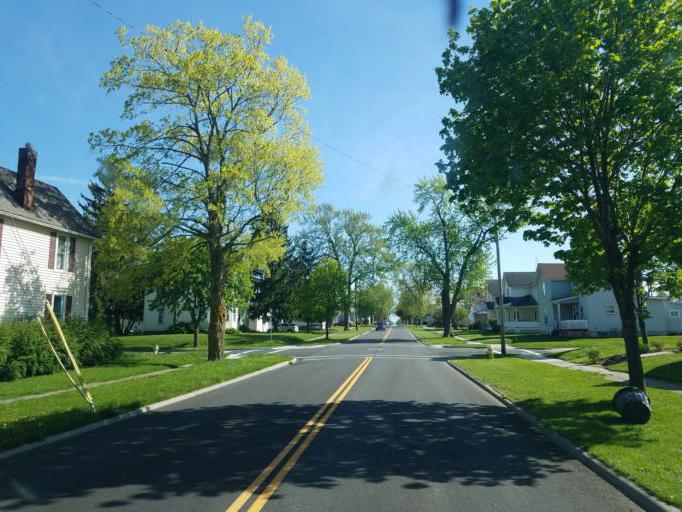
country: US
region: Ohio
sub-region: Huron County
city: Willard
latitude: 41.0577
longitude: -82.7330
